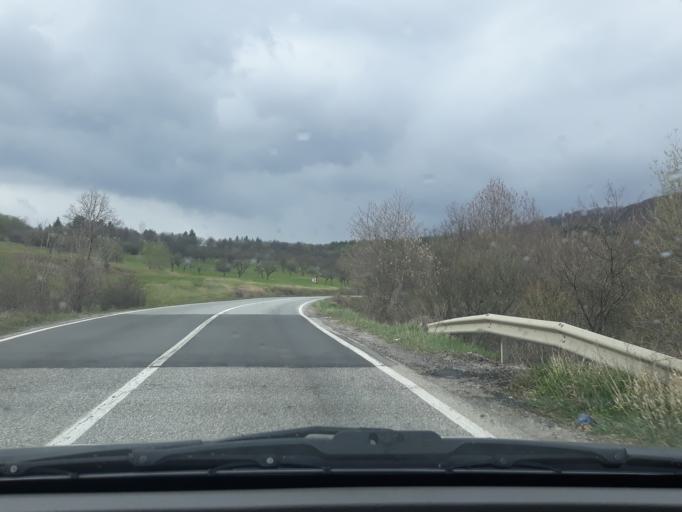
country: RO
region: Harghita
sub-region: Comuna Lupeni
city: Lupeni
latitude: 46.4050
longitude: 25.2136
